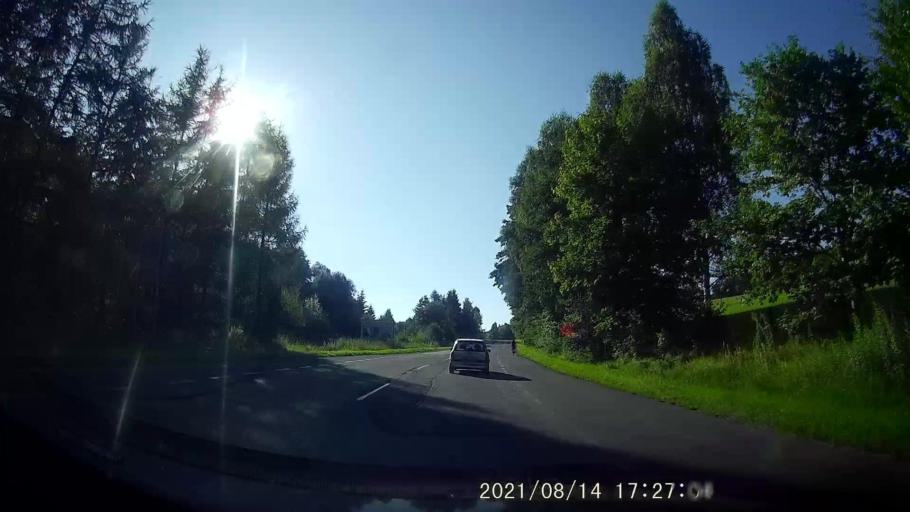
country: PL
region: Lower Silesian Voivodeship
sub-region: Jelenia Gora
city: Jelenia Gora
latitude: 50.9075
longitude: 15.7098
